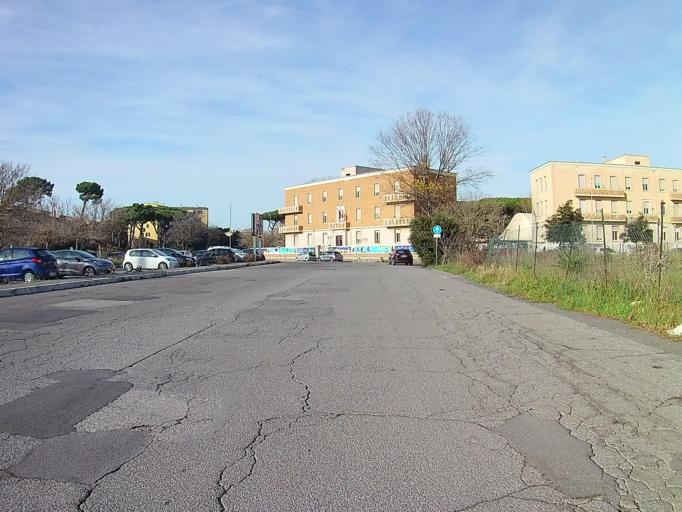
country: IT
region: Latium
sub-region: Citta metropolitana di Roma Capitale
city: Lido di Ostia
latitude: 41.7276
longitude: 12.2972
